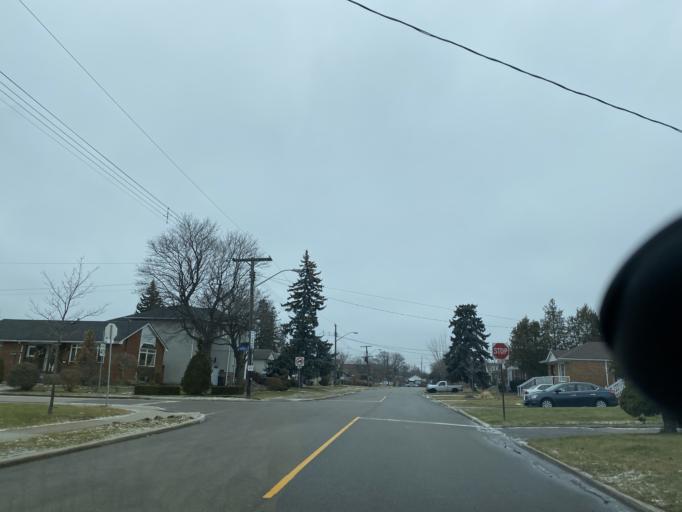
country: CA
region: Ontario
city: Scarborough
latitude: 43.7616
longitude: -79.3091
